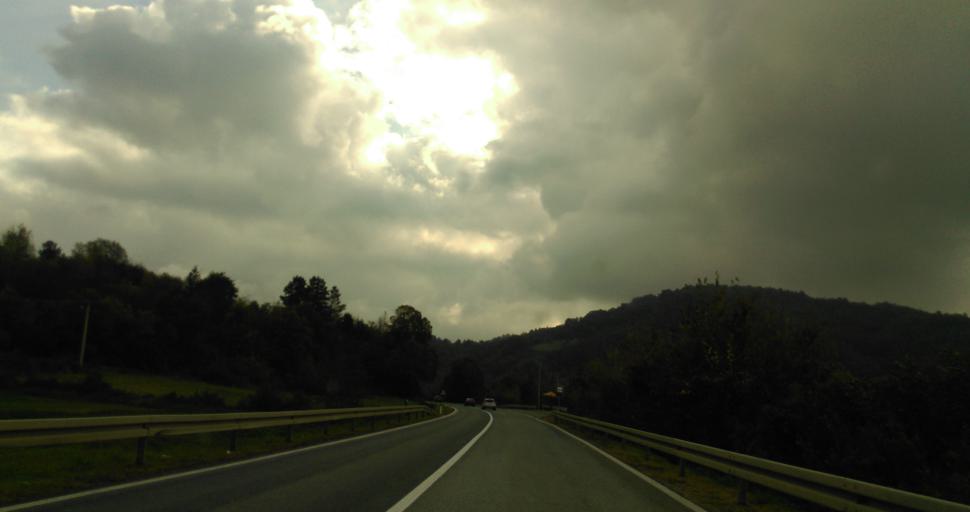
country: RS
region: Central Serbia
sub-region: Kolubarski Okrug
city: Ljig
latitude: 44.1883
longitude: 20.3340
